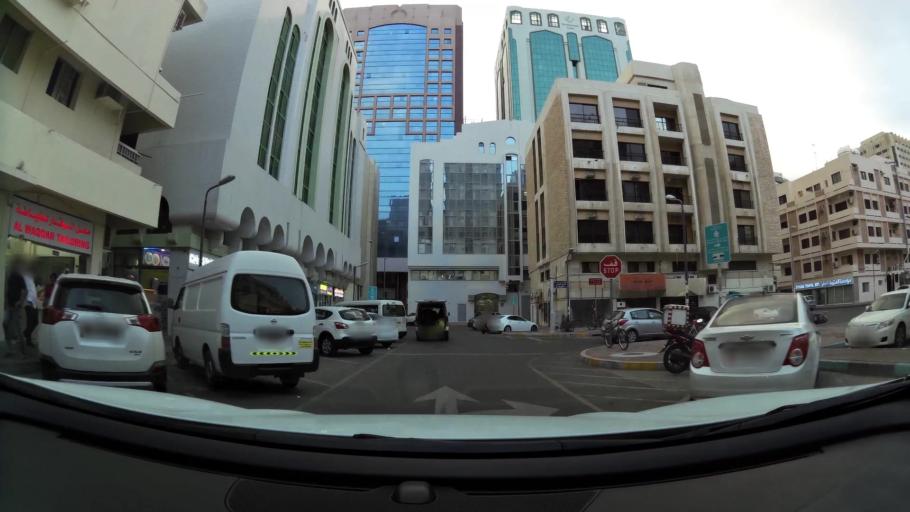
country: AE
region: Abu Dhabi
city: Abu Dhabi
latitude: 24.4931
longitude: 54.3705
